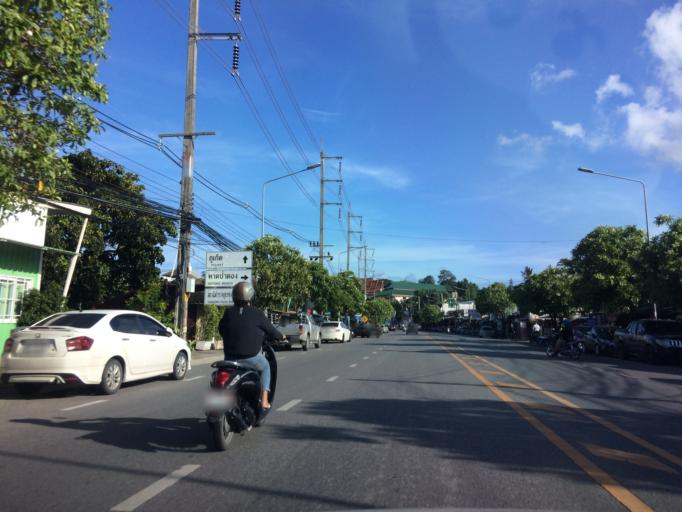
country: TH
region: Phuket
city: Kathu
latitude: 7.9023
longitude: 98.3526
